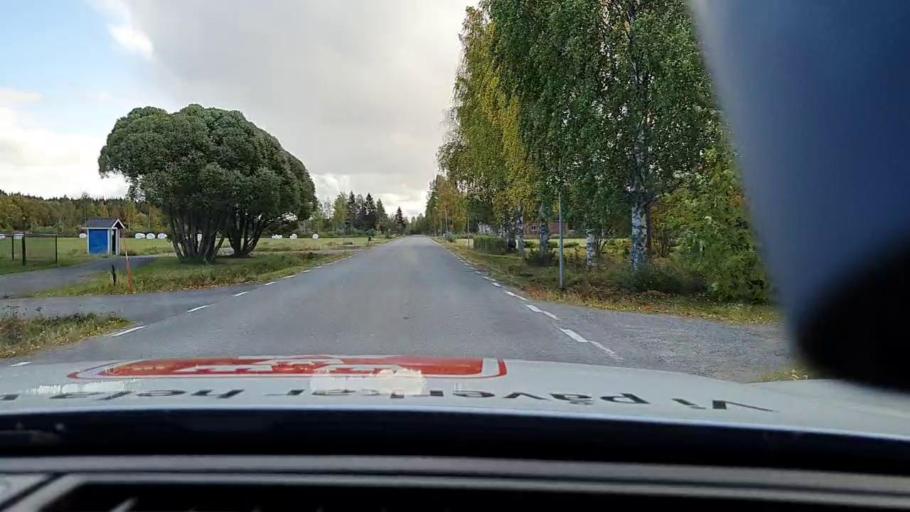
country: SE
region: Vaesterbotten
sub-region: Skelleftea Kommun
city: Langsele
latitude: 64.9503
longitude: 19.9274
